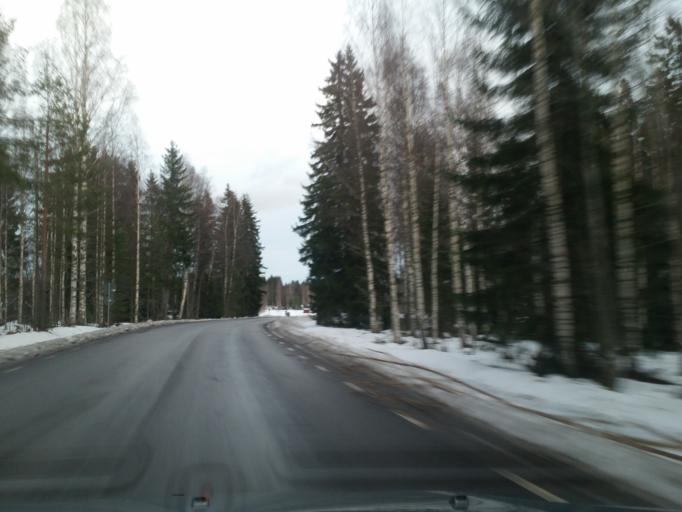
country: SE
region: Gaevleborg
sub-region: Sandvikens Kommun
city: Jarbo
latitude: 60.7630
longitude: 16.5097
